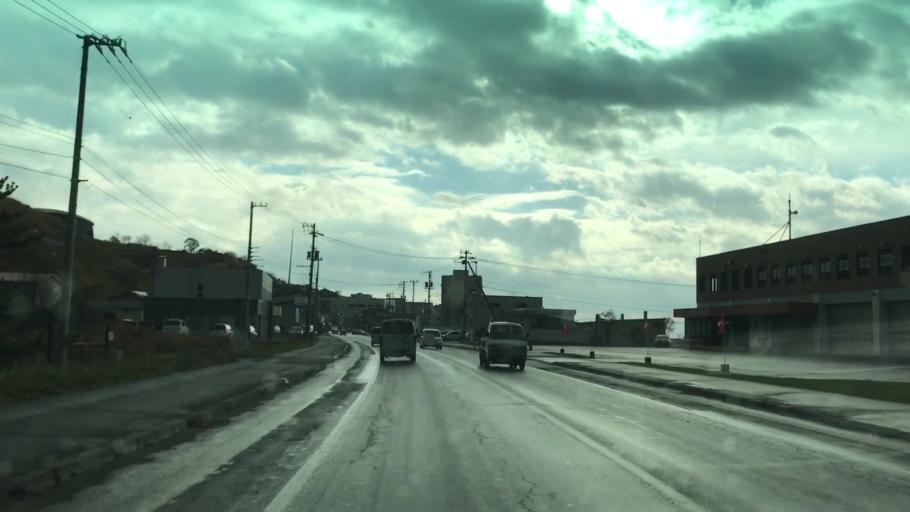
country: JP
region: Hokkaido
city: Shizunai-furukawacho
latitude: 42.1682
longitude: 142.7696
